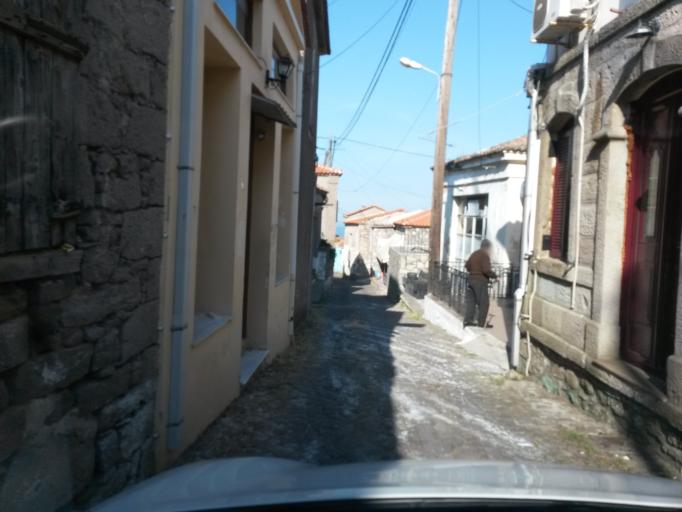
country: GR
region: North Aegean
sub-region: Nomos Lesvou
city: Mantamados
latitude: 39.3466
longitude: 26.3221
